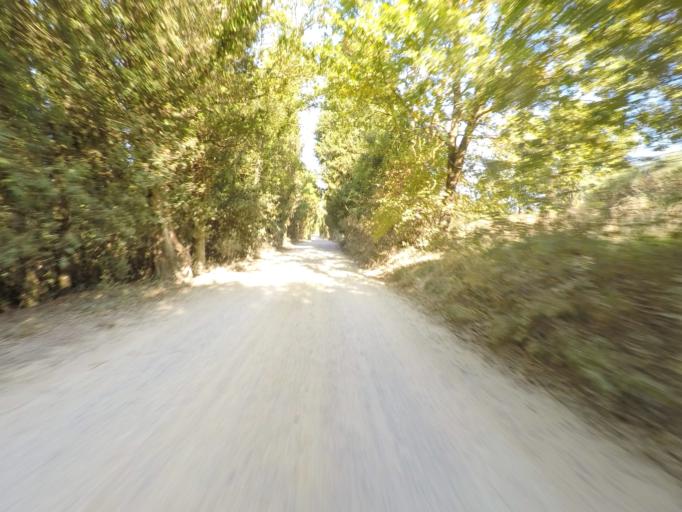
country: IT
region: Tuscany
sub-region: Provincia di Siena
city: Castellina in Chianti
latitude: 43.4320
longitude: 11.3337
